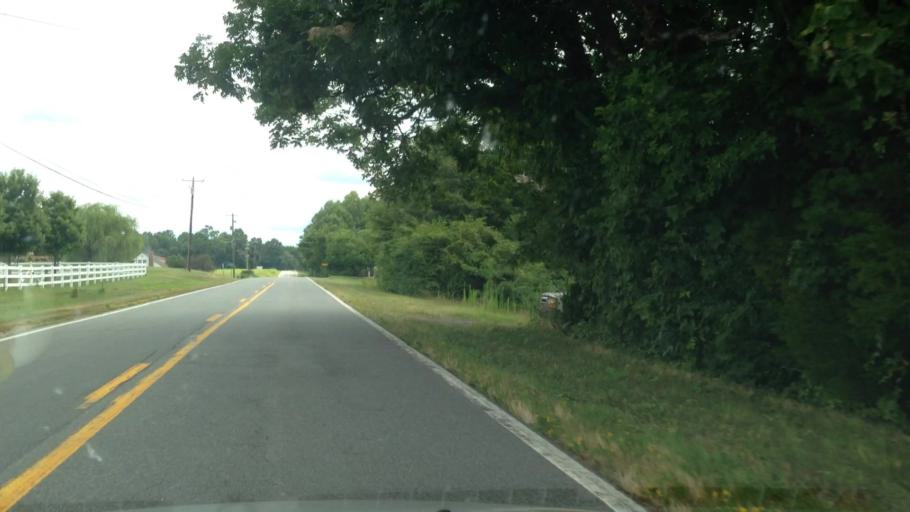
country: US
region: North Carolina
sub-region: Rockingham County
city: Reidsville
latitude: 36.4104
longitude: -79.6132
